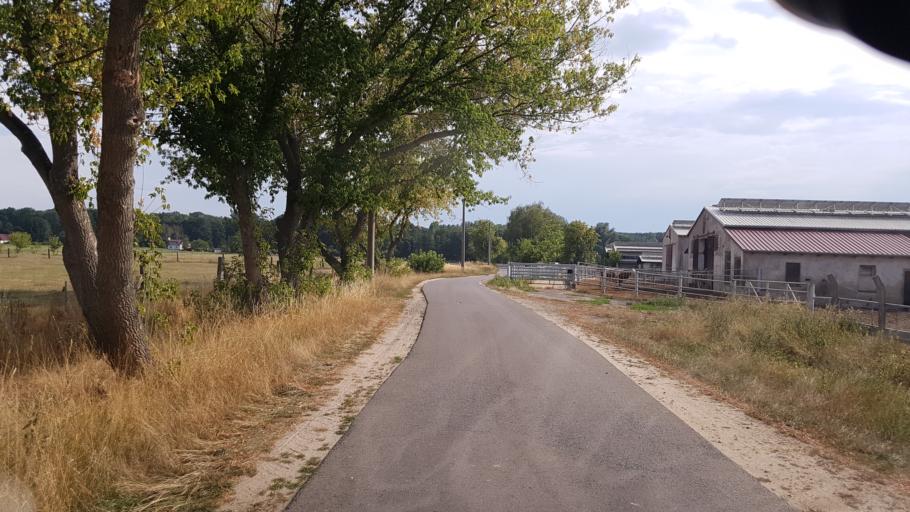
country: DE
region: Brandenburg
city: Hirschfeld
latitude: 51.3888
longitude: 13.6258
